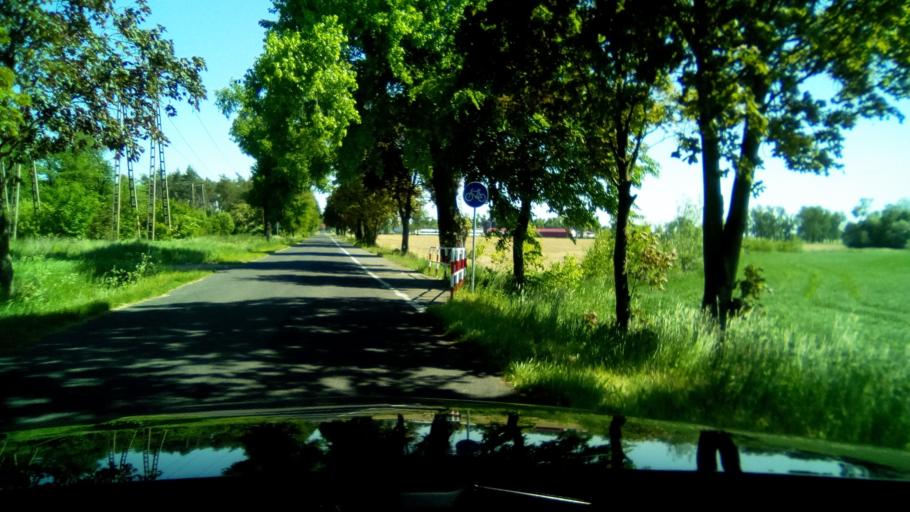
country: PL
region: Greater Poland Voivodeship
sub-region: Powiat gnieznienski
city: Gniezno
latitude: 52.4587
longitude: 17.5690
